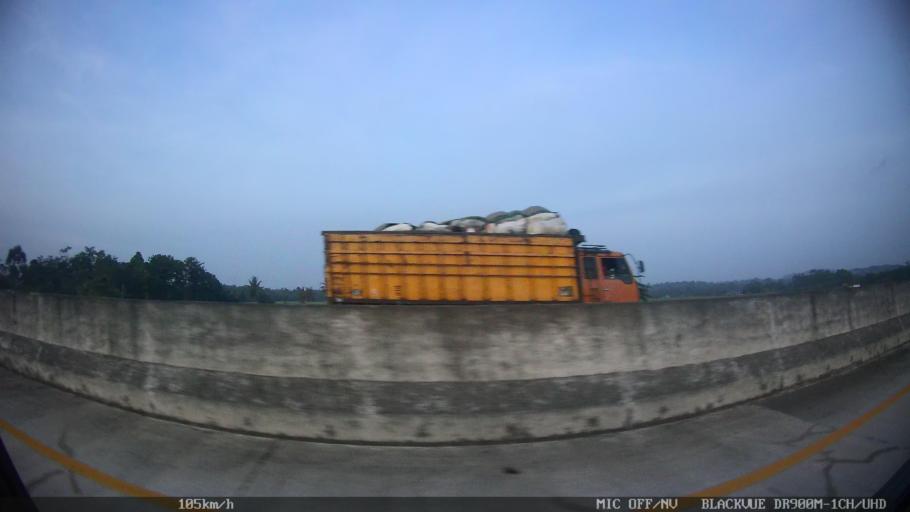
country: ID
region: Lampung
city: Penengahan
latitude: -5.7595
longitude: 105.7116
